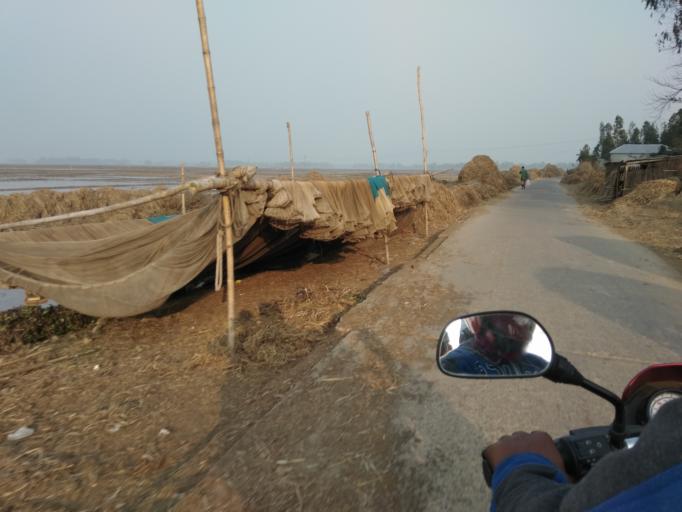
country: BD
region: Rajshahi
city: Ishurdi
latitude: 24.4807
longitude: 89.2357
